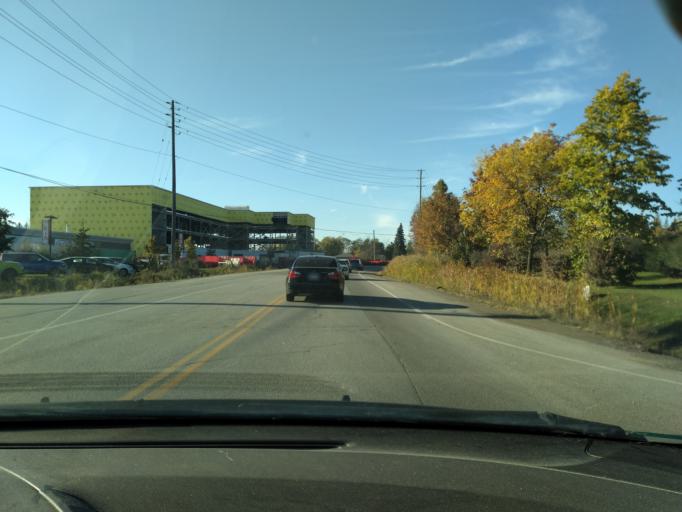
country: CA
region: Ontario
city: Brampton
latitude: 43.8508
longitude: -79.6962
